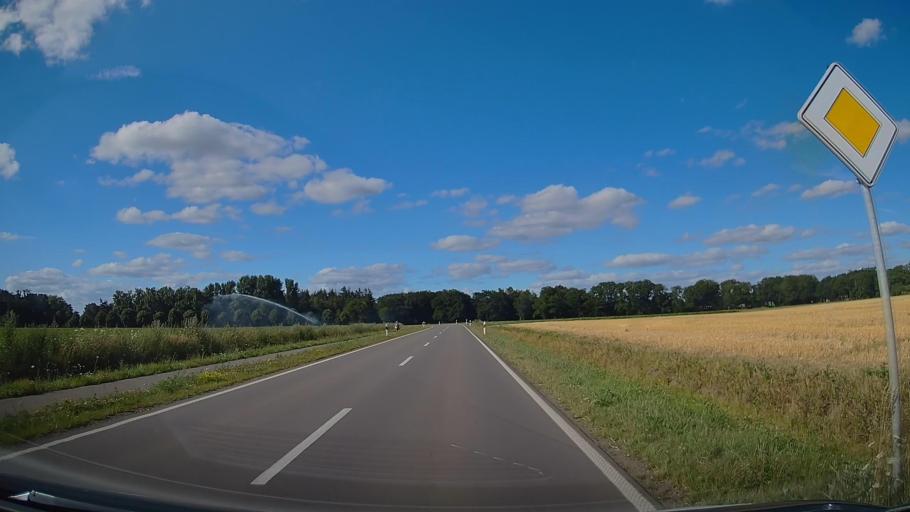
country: DE
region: Lower Saxony
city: Loningen
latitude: 52.7192
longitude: 7.7504
